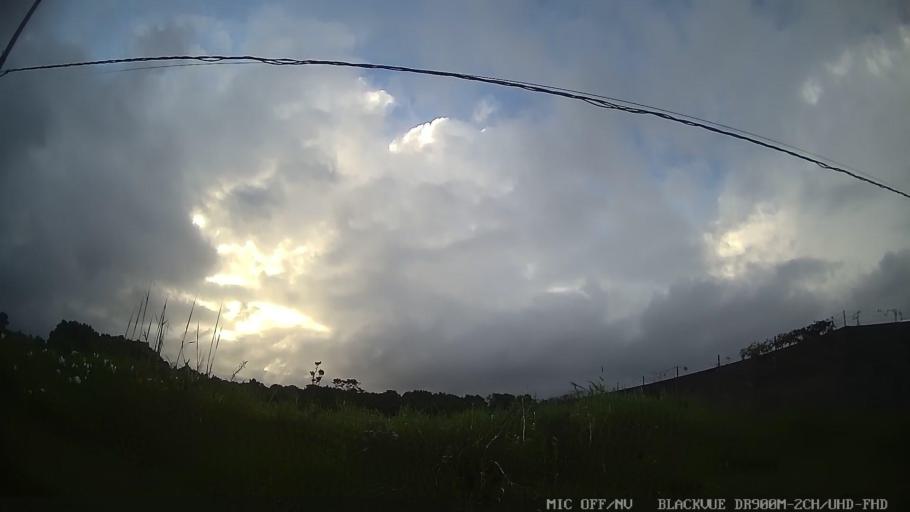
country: BR
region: Sao Paulo
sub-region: Itanhaem
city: Itanhaem
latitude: -24.2077
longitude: -46.8447
